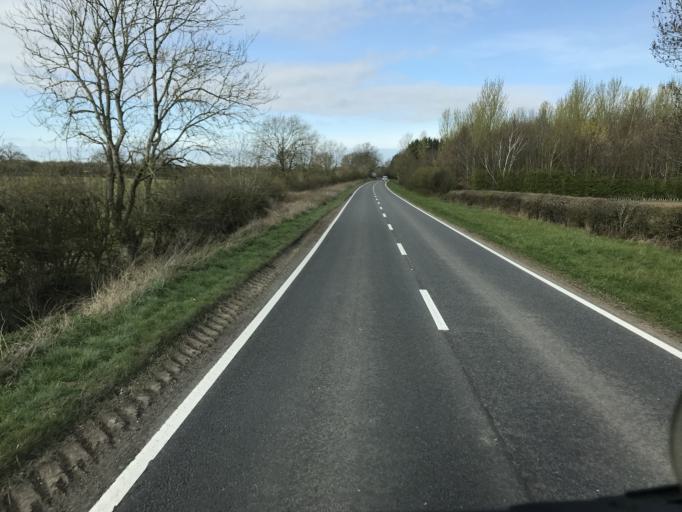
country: GB
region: England
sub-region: Lincolnshire
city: Market Rasen
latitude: 53.3861
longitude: -0.3809
